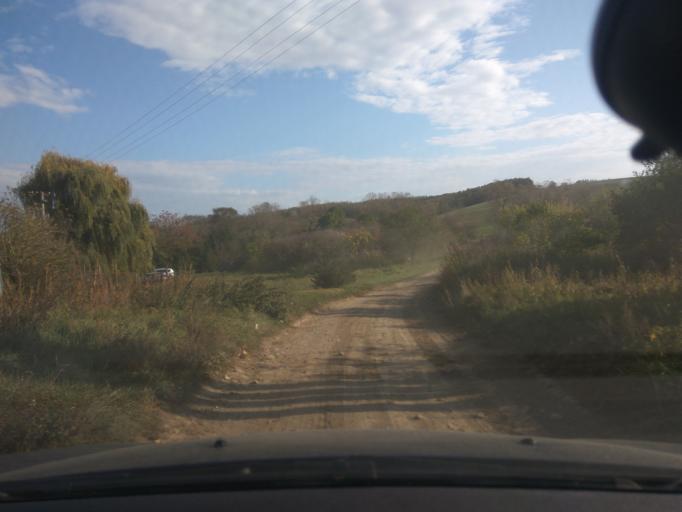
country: SK
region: Trnavsky
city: Hlohovec
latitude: 48.4439
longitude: 17.9258
